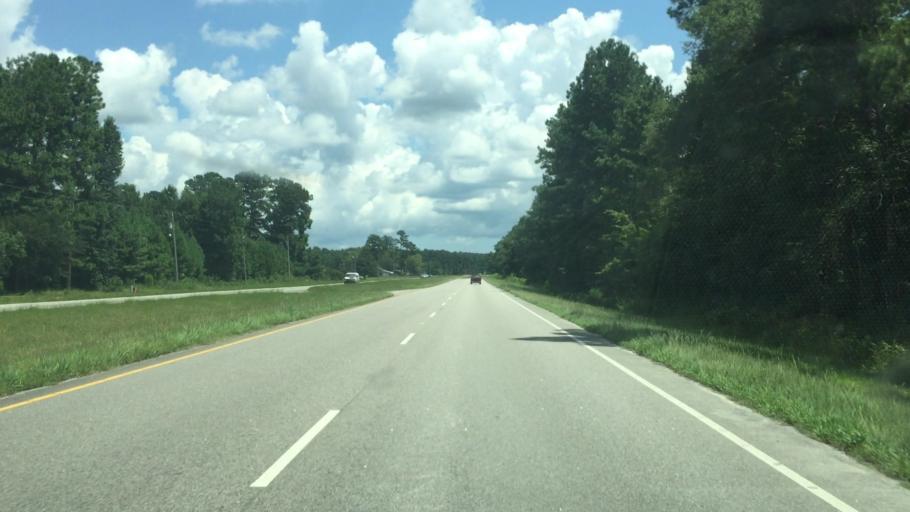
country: US
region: South Carolina
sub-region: Horry County
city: Loris
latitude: 34.0100
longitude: -78.7718
